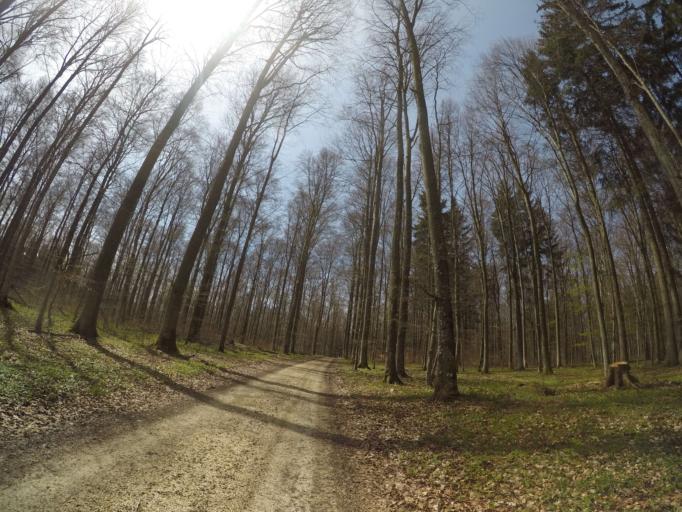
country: DE
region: Baden-Wuerttemberg
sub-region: Regierungsbezirk Stuttgart
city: Neidlingen
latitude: 48.5376
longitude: 9.5726
